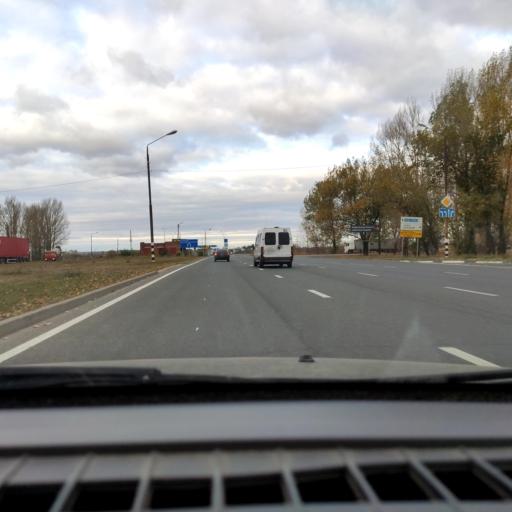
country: RU
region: Samara
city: Podstepki
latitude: 53.5594
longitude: 49.2172
